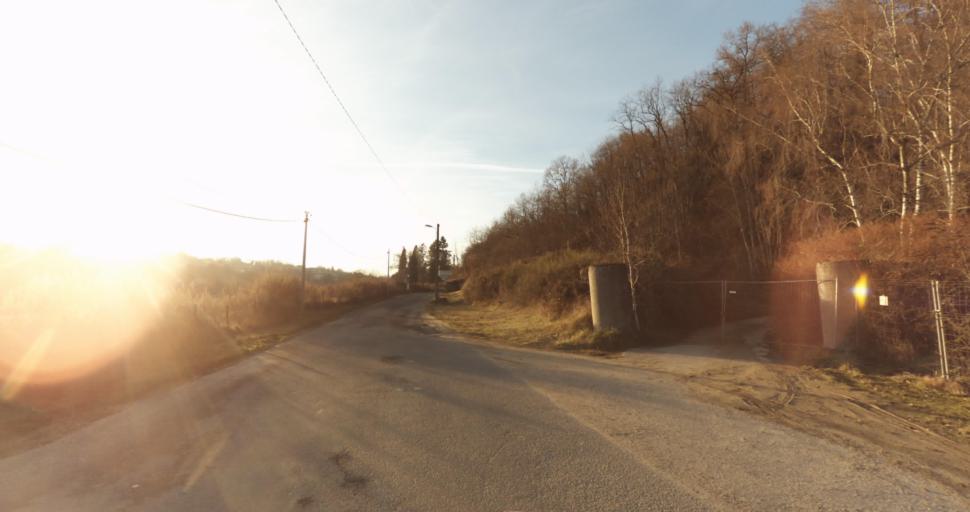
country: FR
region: Limousin
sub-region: Departement de la Haute-Vienne
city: Aixe-sur-Vienne
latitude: 45.8008
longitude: 1.1353
